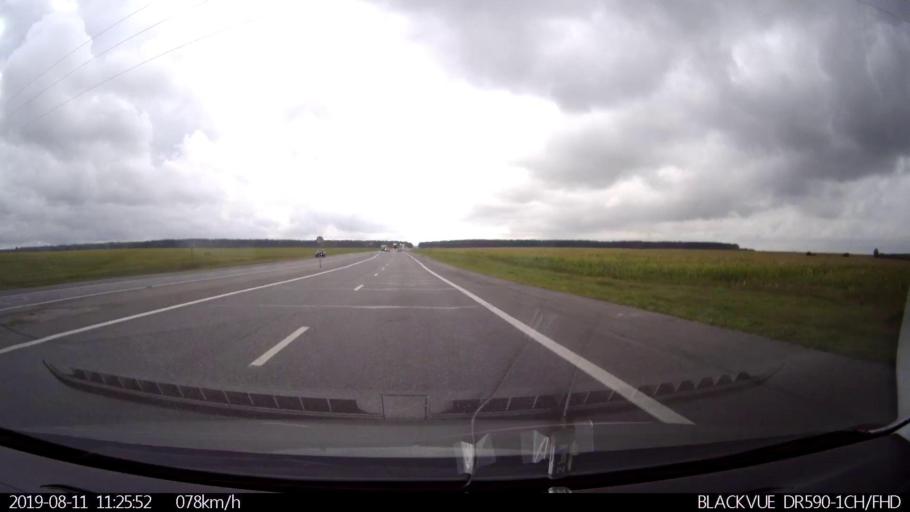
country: RU
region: Ulyanovsk
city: Krasnyy Gulyay
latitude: 54.1123
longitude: 48.2368
